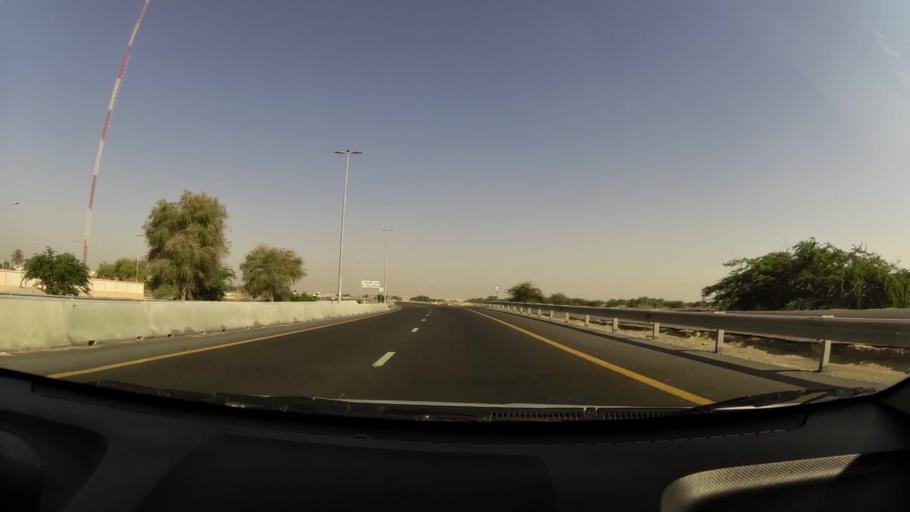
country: AE
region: Umm al Qaywayn
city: Umm al Qaywayn
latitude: 25.4871
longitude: 55.5535
